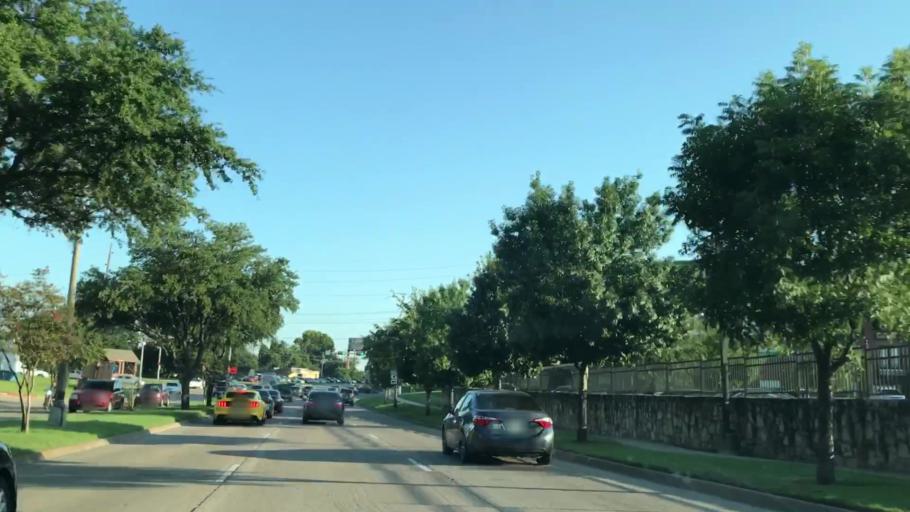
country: US
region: Texas
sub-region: Denton County
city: Denton
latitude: 33.2053
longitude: -97.1364
